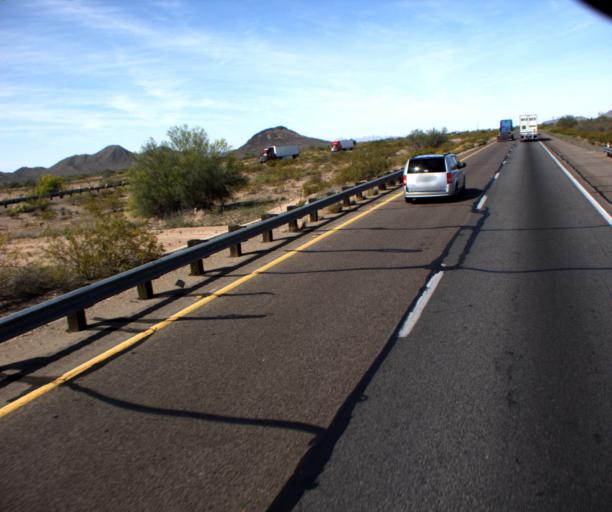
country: US
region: Arizona
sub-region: Maricopa County
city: Buckeye
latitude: 33.5079
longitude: -112.9929
